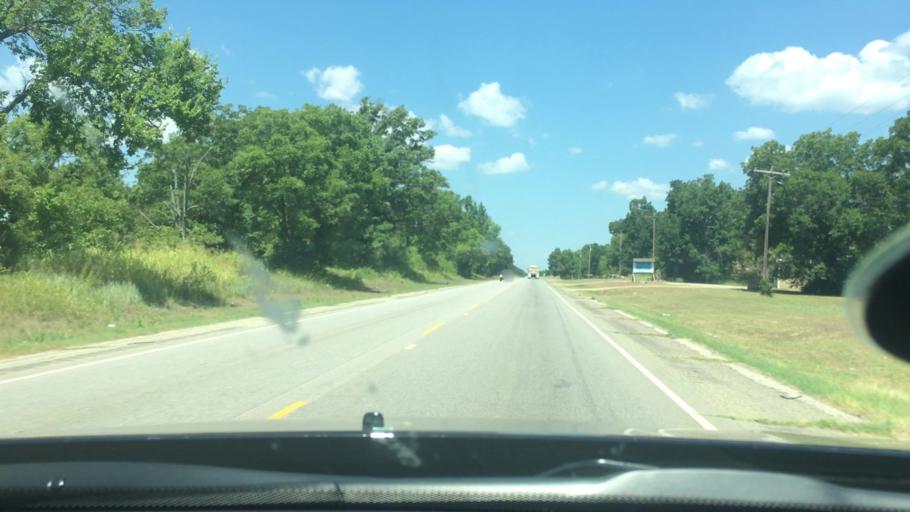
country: US
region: Oklahoma
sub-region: Marshall County
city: Oakland
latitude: 34.1425
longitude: -96.8043
